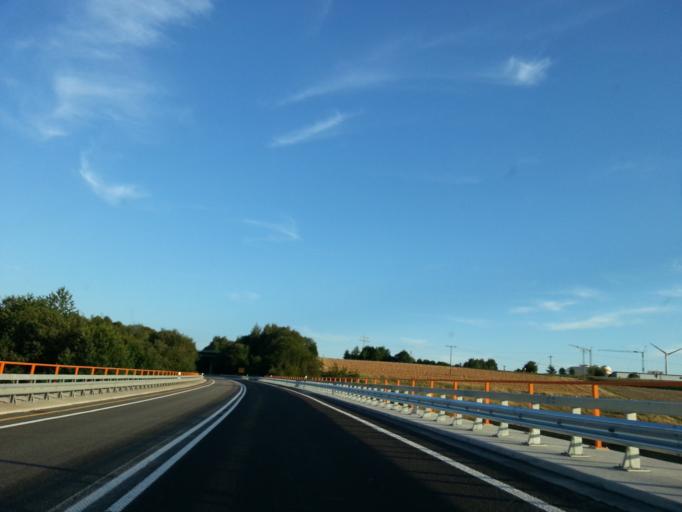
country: DE
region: Rheinland-Pfalz
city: Weselberg
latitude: 49.3357
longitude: 7.6007
